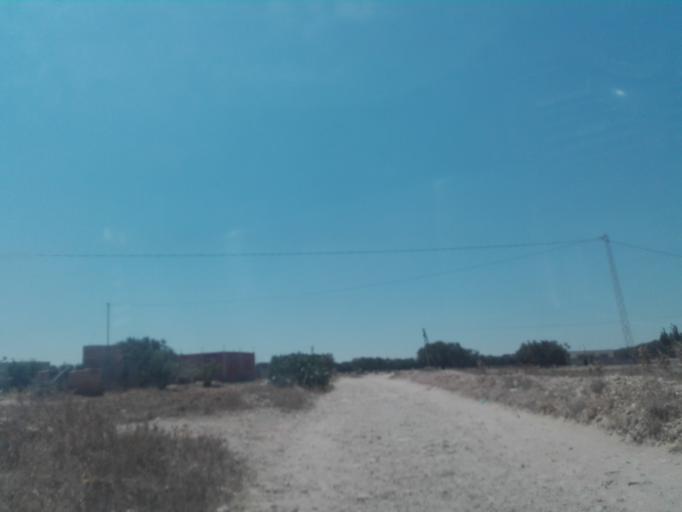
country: TN
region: Safaqis
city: Jabinyanah
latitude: 35.0828
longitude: 10.9617
